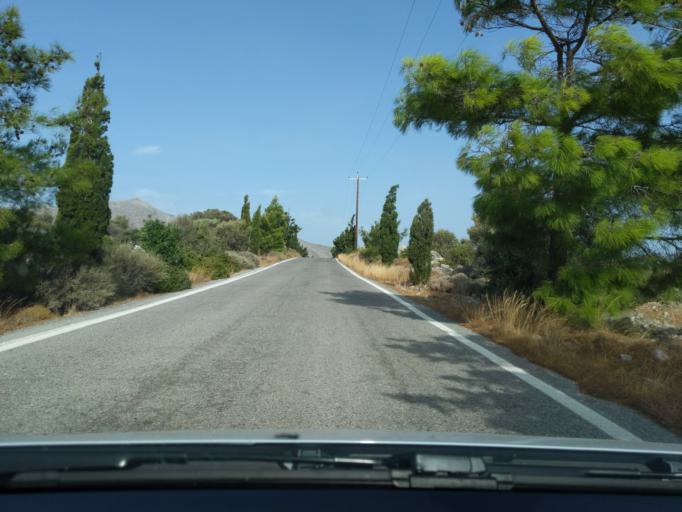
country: GR
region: Crete
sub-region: Nomos Lasithiou
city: Palekastro
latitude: 35.0894
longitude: 26.2405
